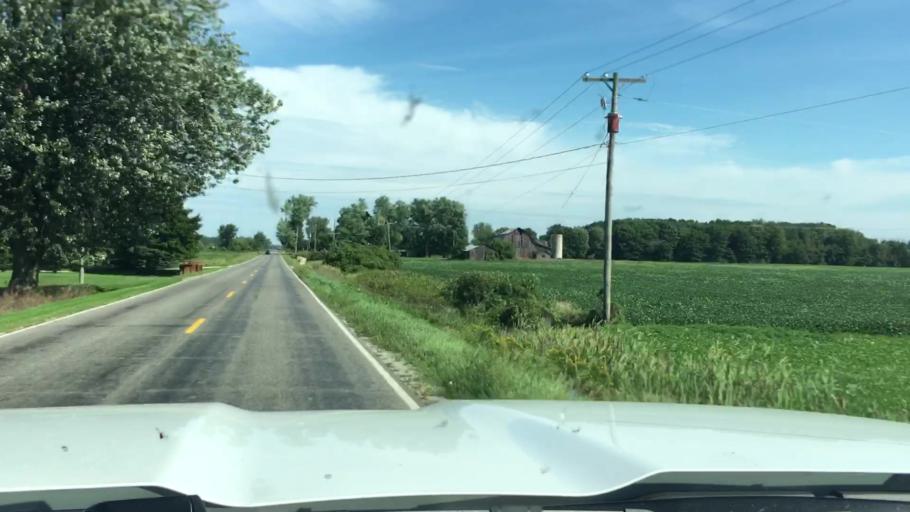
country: US
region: Michigan
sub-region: Saginaw County
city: Hemlock
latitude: 43.4881
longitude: -84.2299
